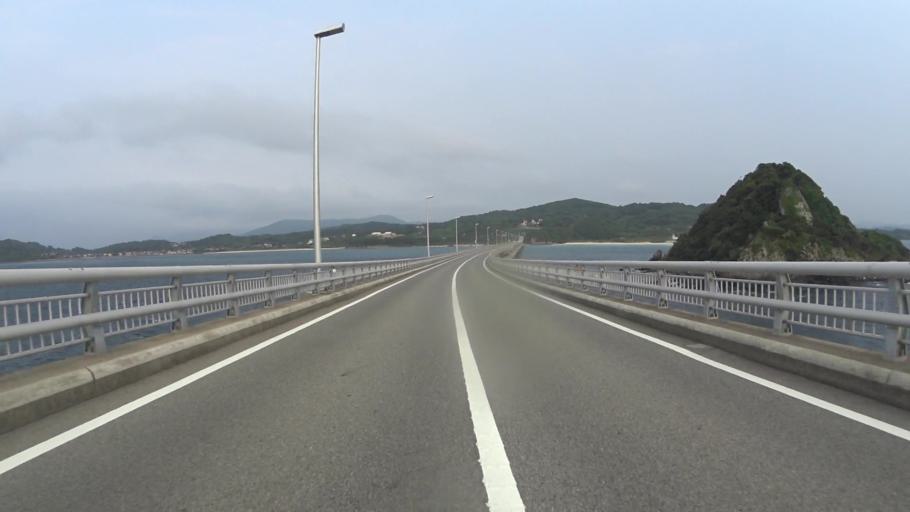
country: JP
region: Yamaguchi
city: Nagato
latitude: 34.3537
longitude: 130.8852
